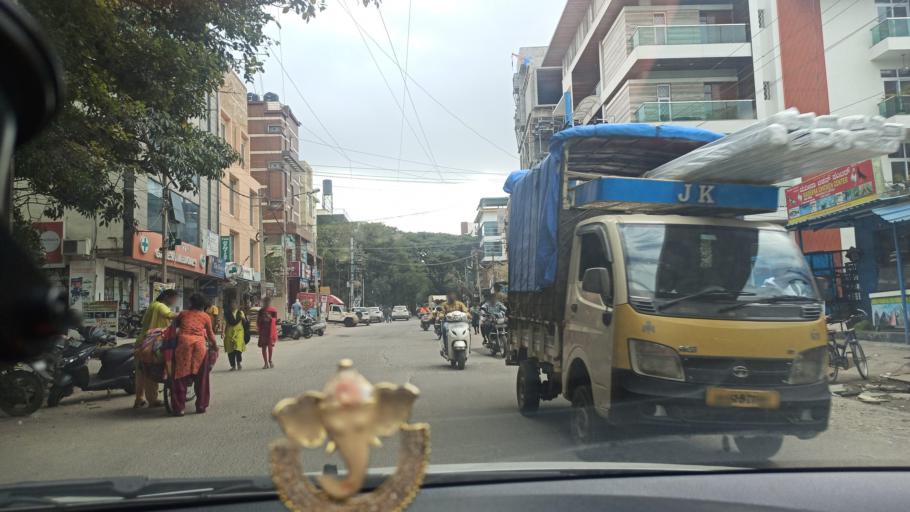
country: IN
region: Karnataka
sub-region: Bangalore Urban
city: Bangalore
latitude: 12.9194
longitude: 77.6492
